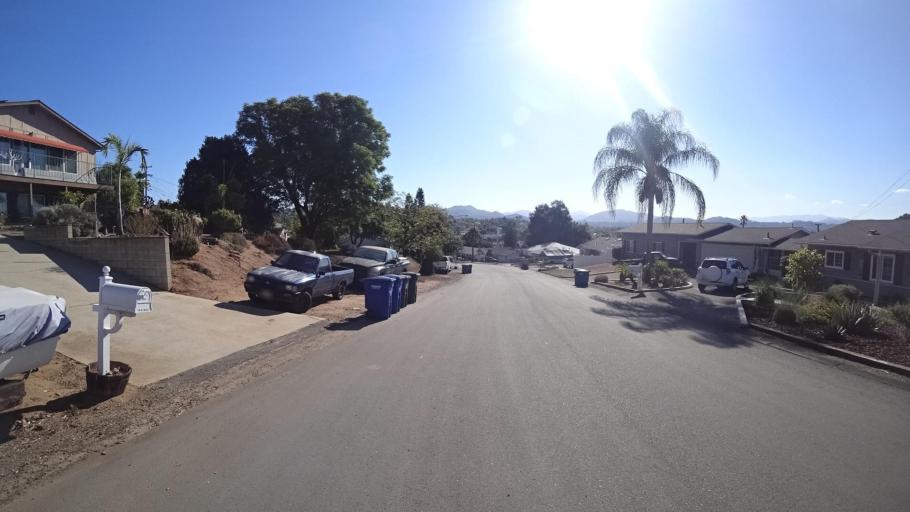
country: US
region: California
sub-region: San Diego County
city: Bostonia
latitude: 32.8176
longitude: -116.9400
